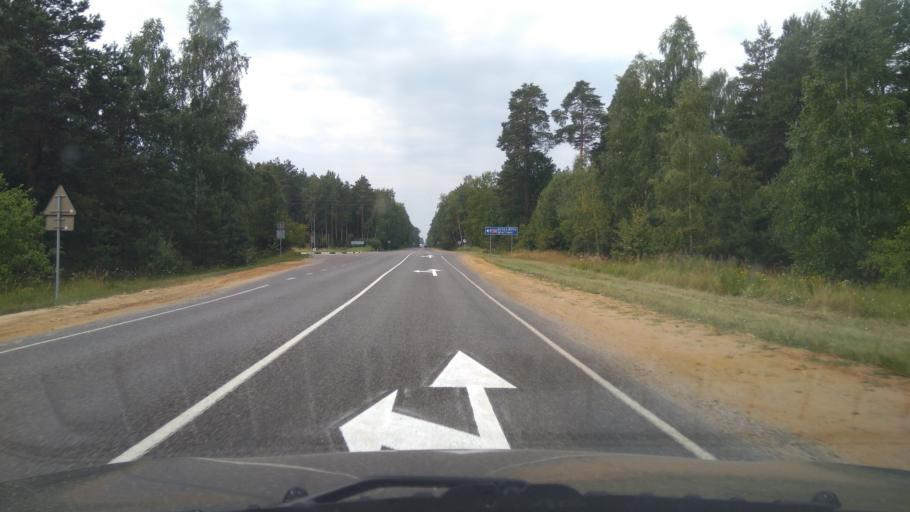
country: BY
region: Brest
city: Nyakhachava
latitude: 52.5888
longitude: 25.0943
